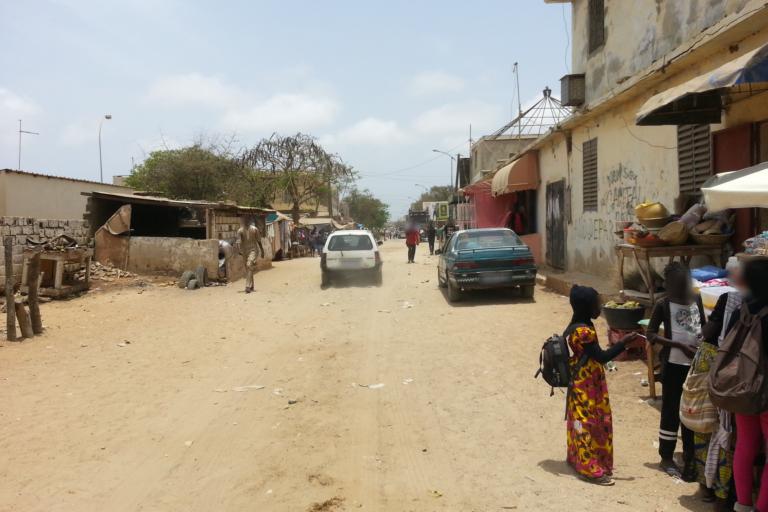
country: SN
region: Dakar
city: Pikine
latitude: 14.7817
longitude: -17.3716
